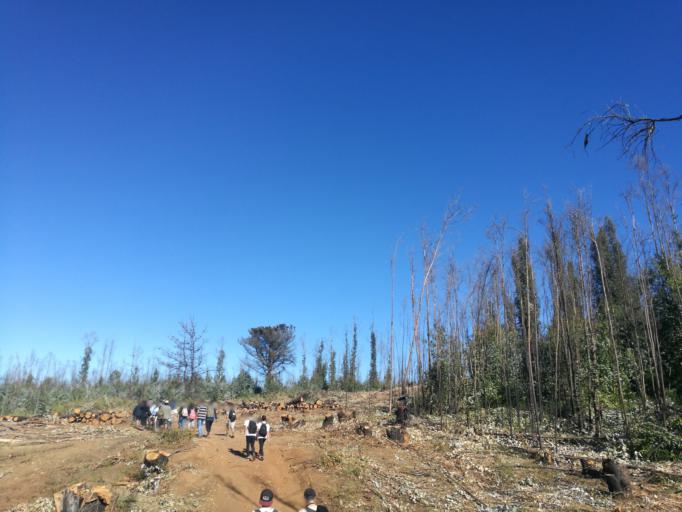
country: CL
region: Valparaiso
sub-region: Provincia de Valparaiso
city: Valparaiso
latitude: -33.0712
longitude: -71.6474
